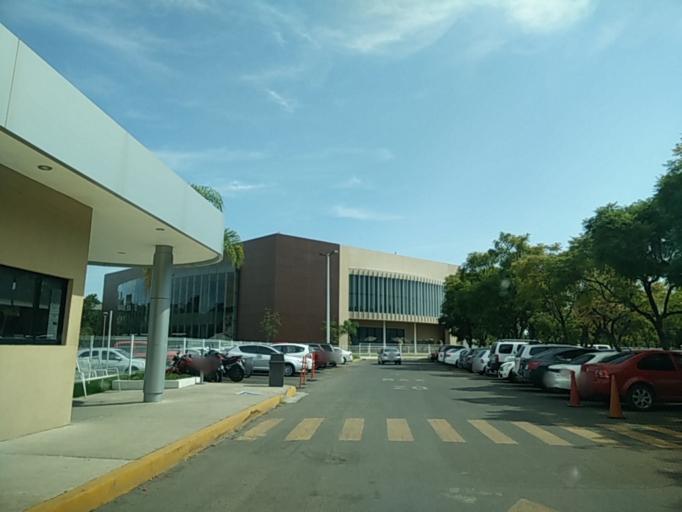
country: MX
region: Jalisco
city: Nuevo Mexico
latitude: 20.7328
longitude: -103.4570
